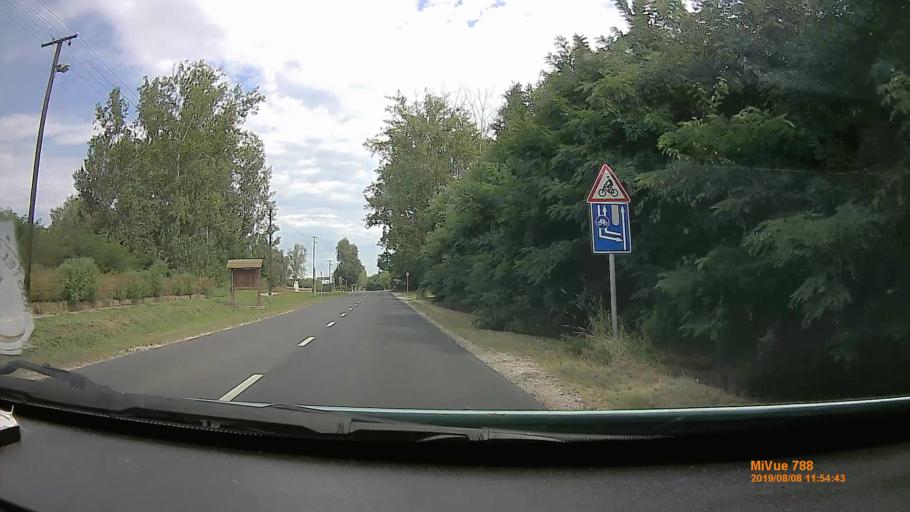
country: HU
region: Szabolcs-Szatmar-Bereg
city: Nyirmihalydi
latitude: 47.7357
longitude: 21.9725
